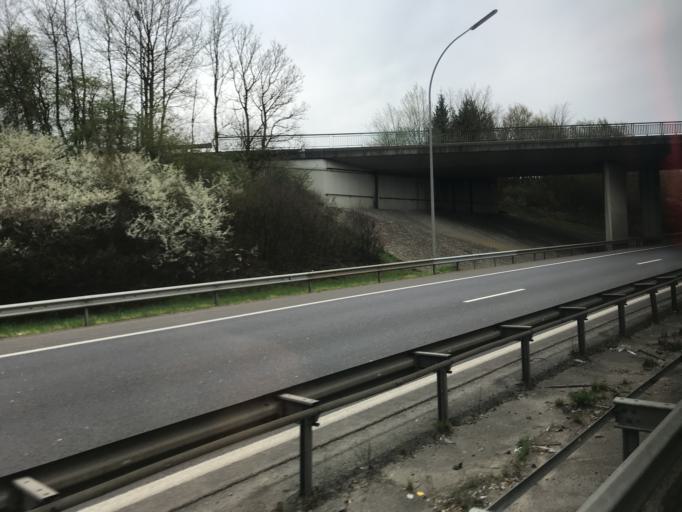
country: LU
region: Luxembourg
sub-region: Canton d'Esch-sur-Alzette
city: Leudelange
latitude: 49.5676
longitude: 6.0860
